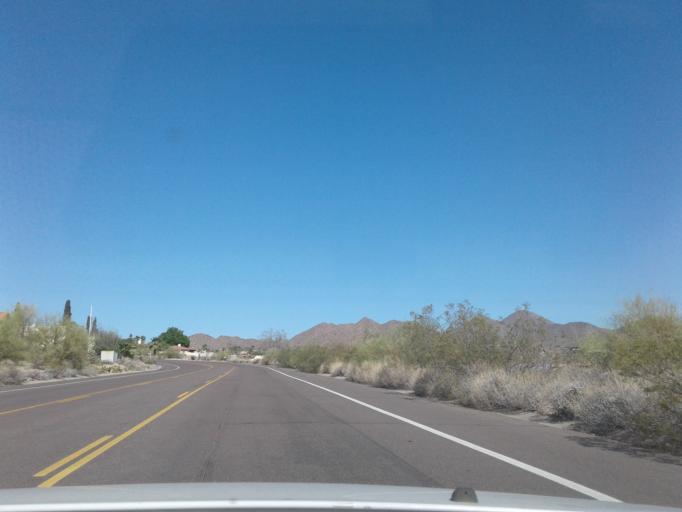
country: US
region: Arizona
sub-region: Maricopa County
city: Fountain Hills
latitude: 33.5912
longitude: -111.7435
